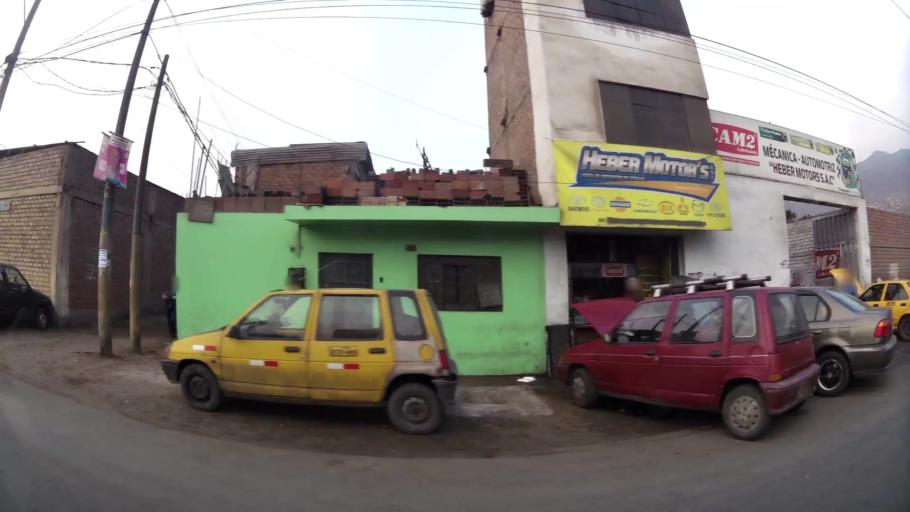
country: PE
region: Lima
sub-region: Lima
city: Independencia
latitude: -11.9876
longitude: -76.9987
